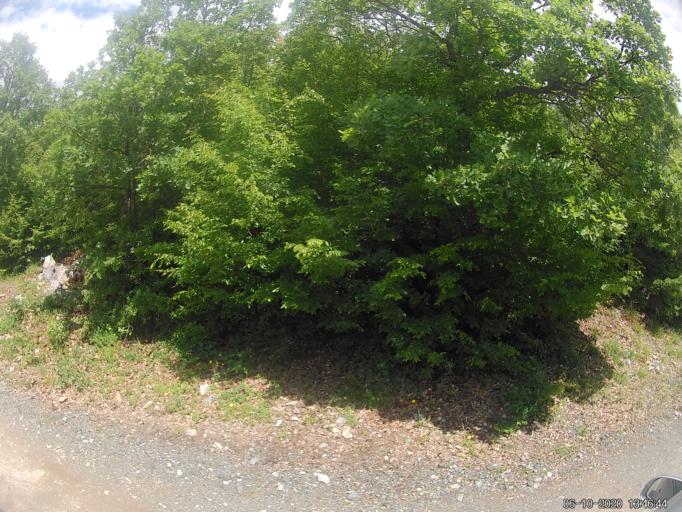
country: XK
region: Prizren
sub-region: Komuna e Therandes
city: Budakovo
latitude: 42.4076
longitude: 20.9164
